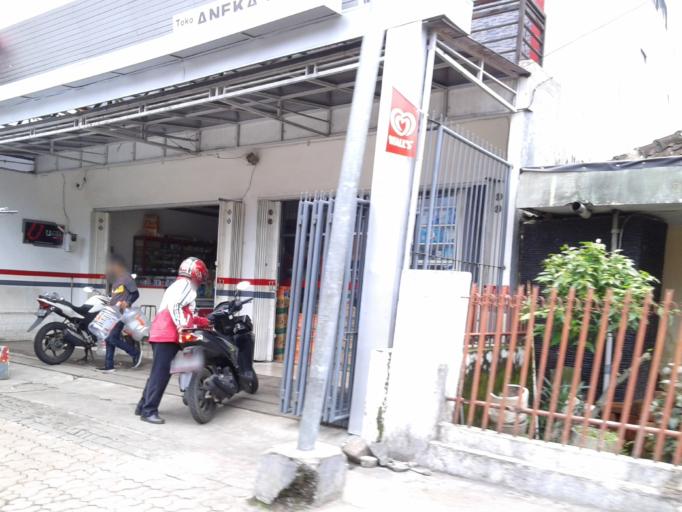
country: ID
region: East Java
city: Singosari
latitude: -7.8917
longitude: 112.6672
